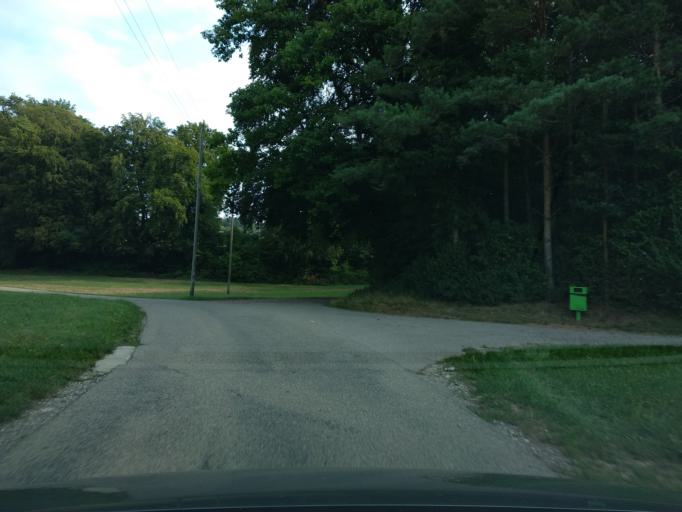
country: CH
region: Zurich
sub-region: Bezirk Andelfingen
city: Marthalen
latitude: 47.6434
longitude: 8.6760
